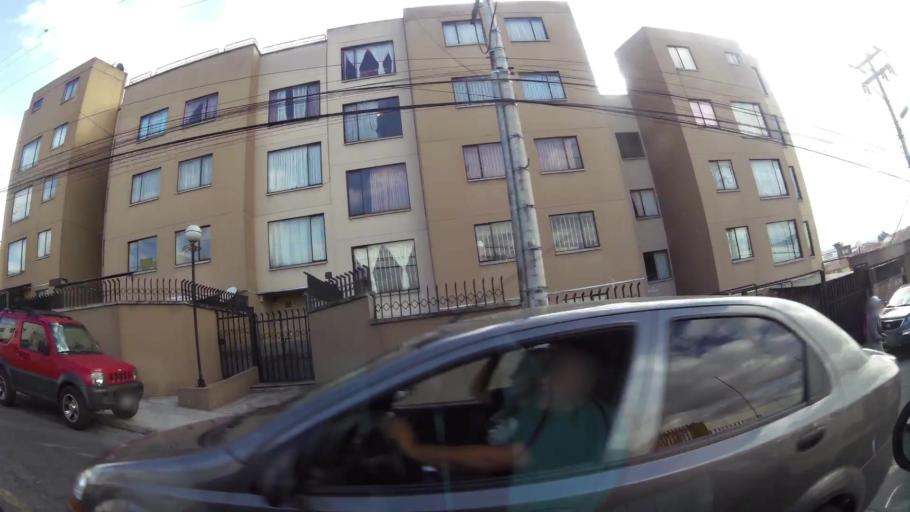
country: EC
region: Pichincha
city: Quito
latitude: -0.1297
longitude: -78.4726
